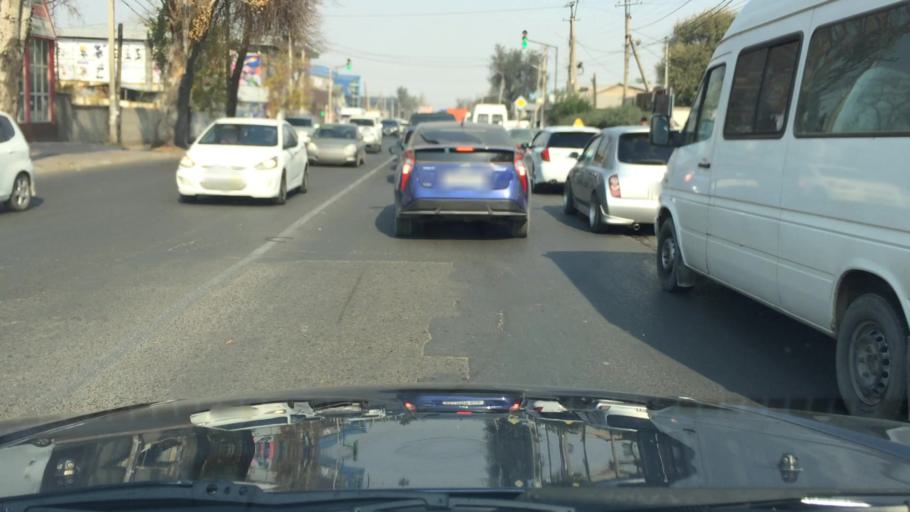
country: KG
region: Chuy
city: Lebedinovka
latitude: 42.8792
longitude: 74.6375
